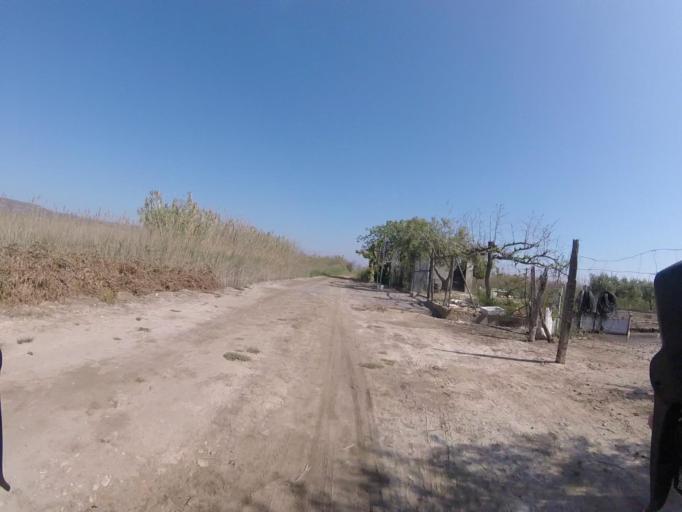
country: ES
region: Valencia
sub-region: Provincia de Castello
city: Torreblanca
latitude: 40.1680
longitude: 0.1733
